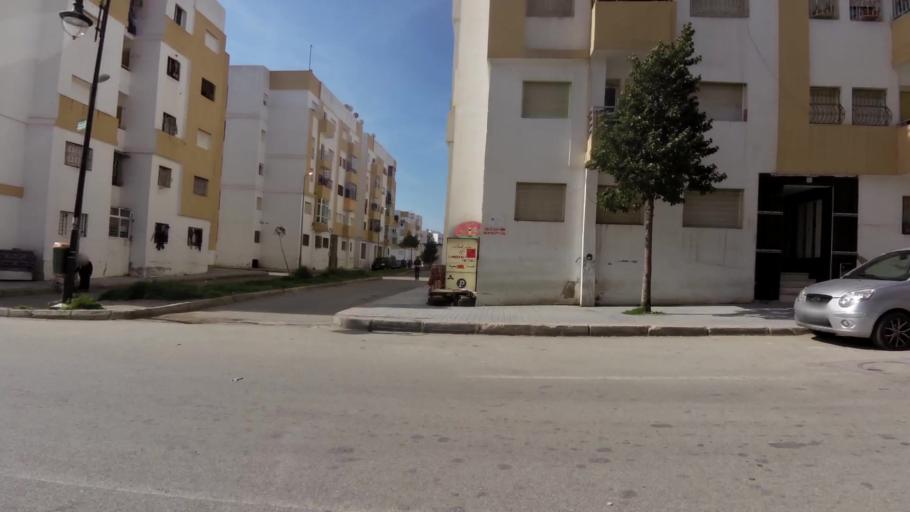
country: MA
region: Tanger-Tetouan
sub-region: Tanger-Assilah
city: Tangier
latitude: 35.7247
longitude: -5.8086
